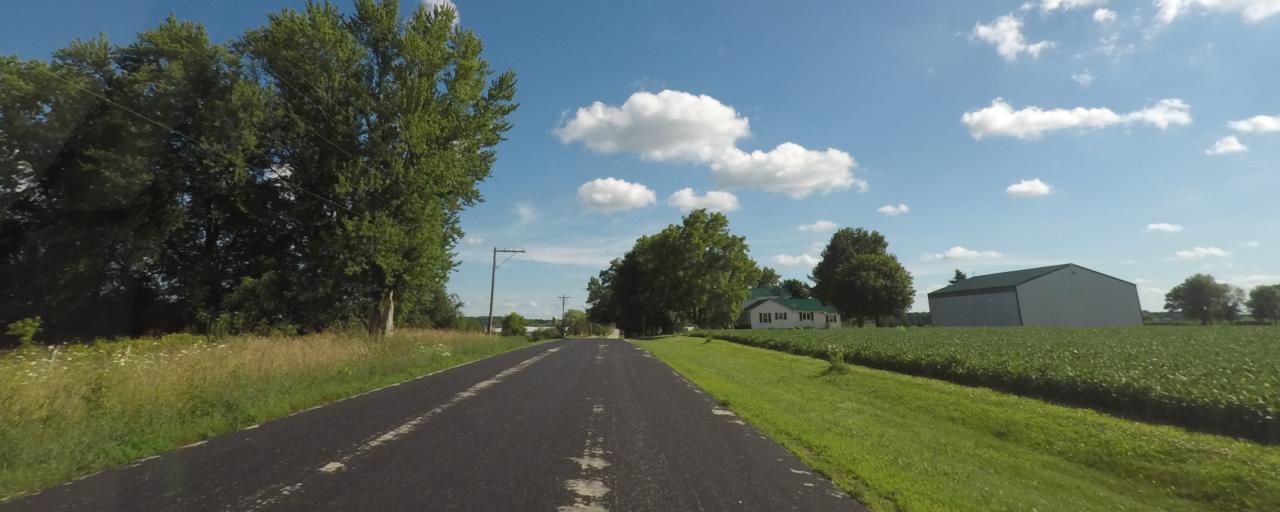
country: US
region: Wisconsin
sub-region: Rock County
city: Edgerton
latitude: 42.8493
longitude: -89.1320
